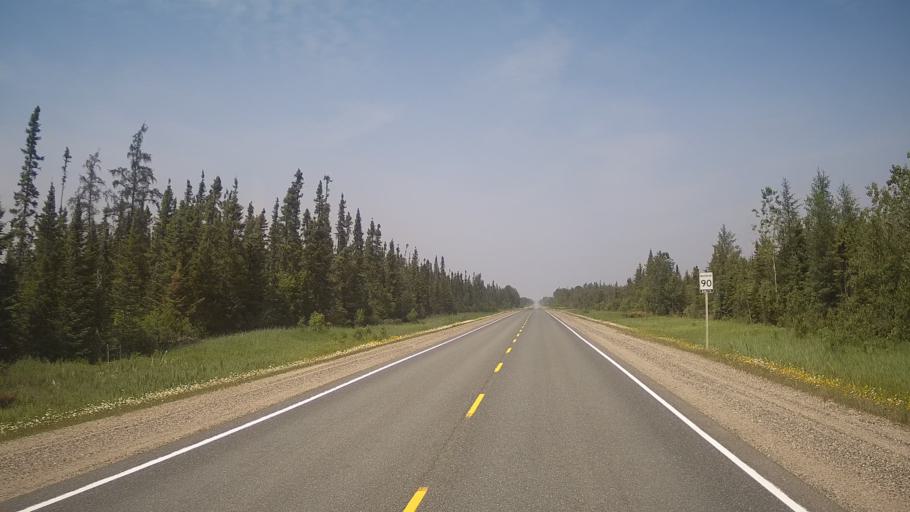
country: CA
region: Ontario
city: Timmins
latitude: 48.7934
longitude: -81.3663
